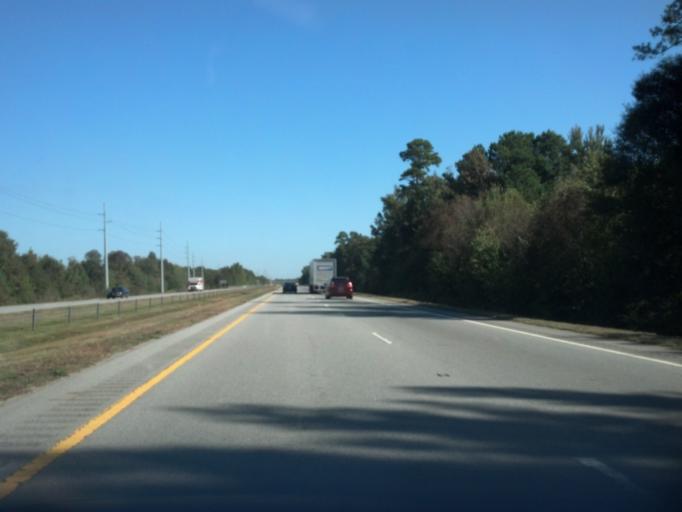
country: US
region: North Carolina
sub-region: Pitt County
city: Greenville
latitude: 35.6393
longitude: -77.4263
